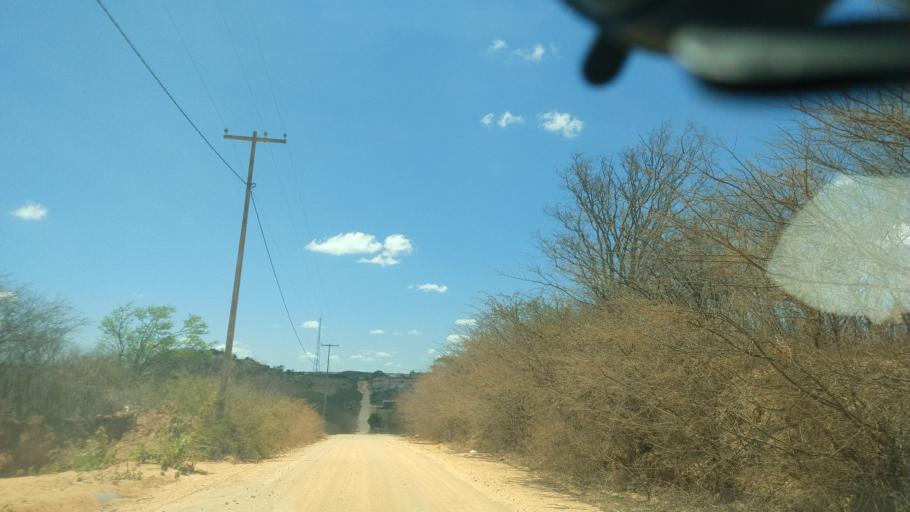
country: BR
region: Rio Grande do Norte
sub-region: Cerro Cora
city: Cerro Cora
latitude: -6.0298
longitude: -36.3403
